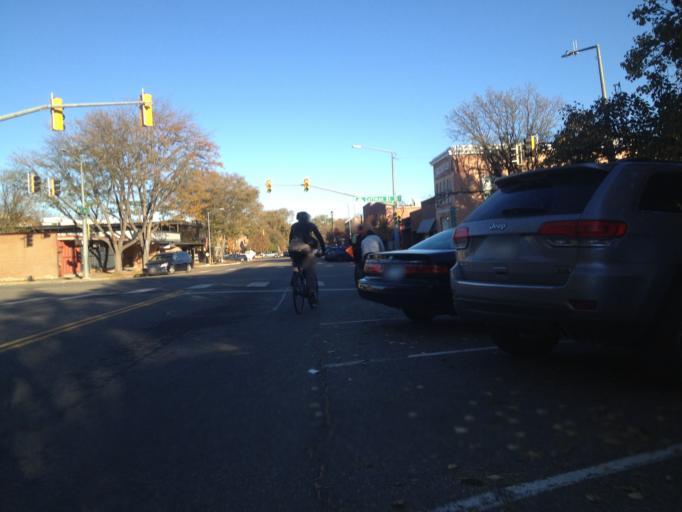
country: US
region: Colorado
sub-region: Boulder County
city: Longmont
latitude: 40.1657
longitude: -105.1043
